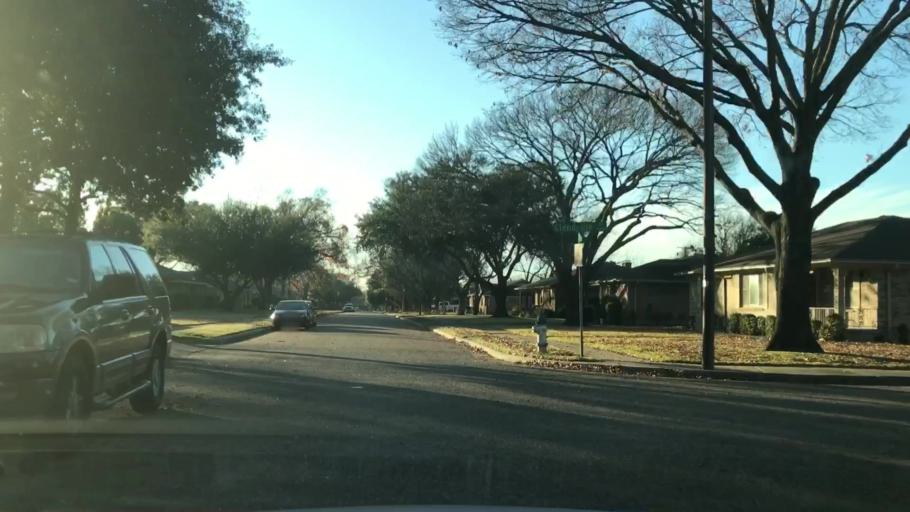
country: US
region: Texas
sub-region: Dallas County
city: Highland Park
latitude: 32.7960
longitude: -96.7007
